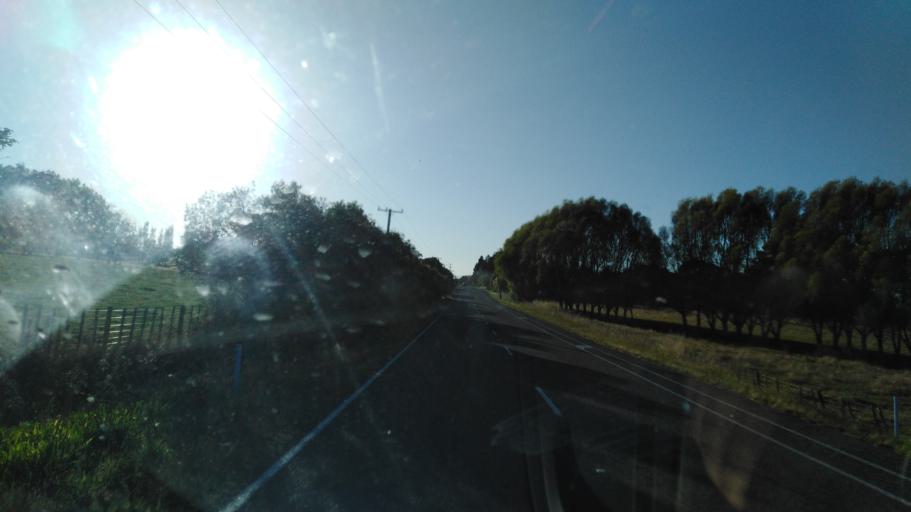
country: NZ
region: Manawatu-Wanganui
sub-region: Rangitikei District
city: Bulls
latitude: -40.0646
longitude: 175.3879
